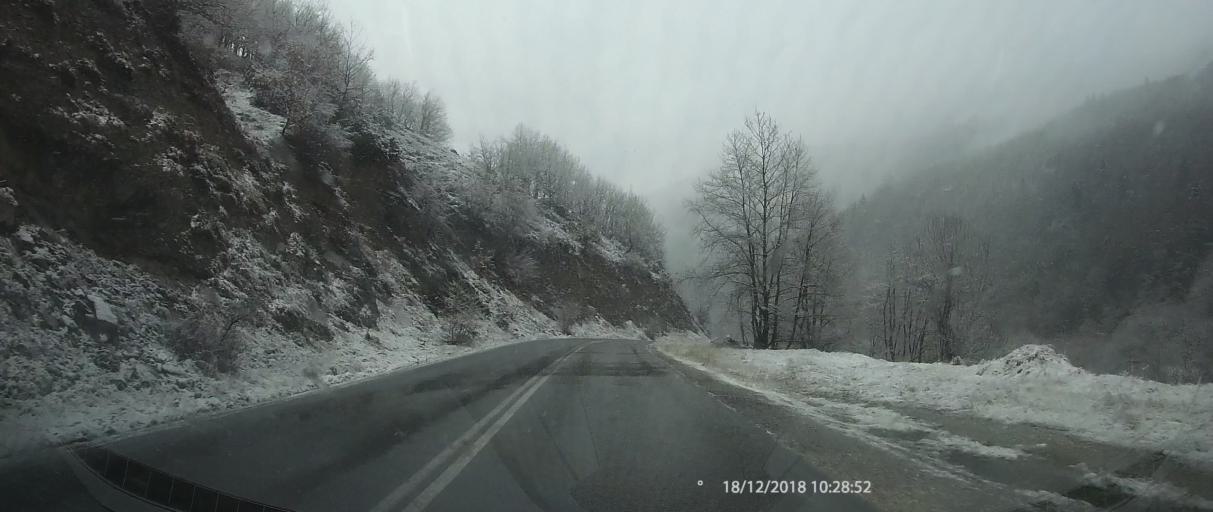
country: GR
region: Central Macedonia
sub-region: Nomos Pierias
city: Kato Milia
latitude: 40.1798
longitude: 22.2657
